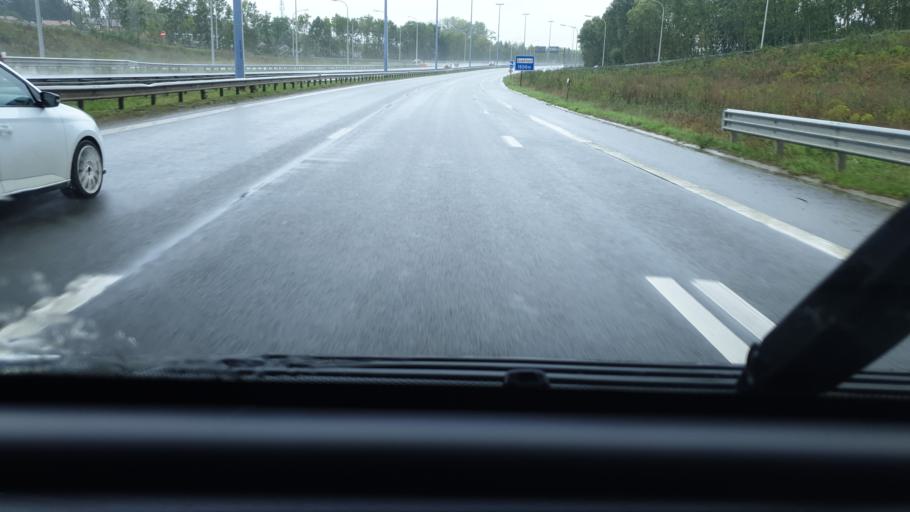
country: BE
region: Wallonia
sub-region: Province du Hainaut
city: Chatelet
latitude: 50.4215
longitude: 4.4969
